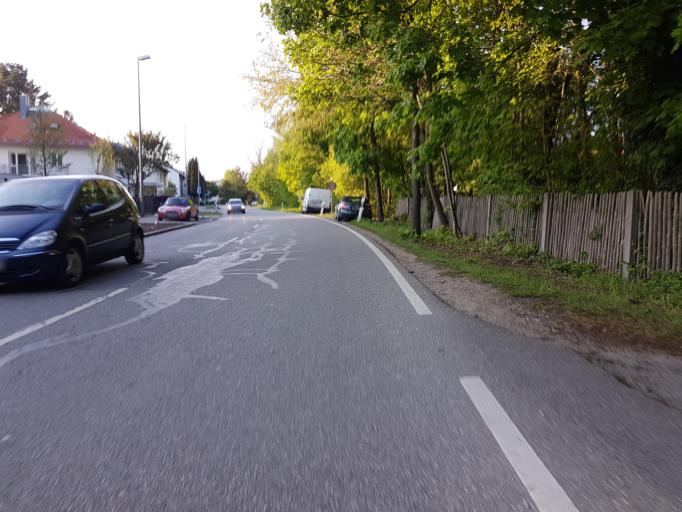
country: DE
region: Bavaria
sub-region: Upper Bavaria
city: Pasing
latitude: 48.1734
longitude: 11.4606
